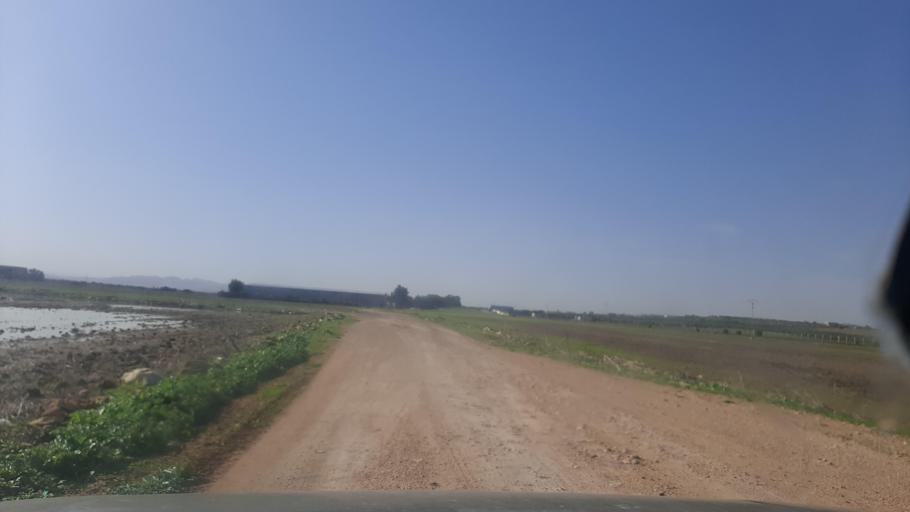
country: TN
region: Tunis
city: La Mohammedia
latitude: 36.6482
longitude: 10.0867
